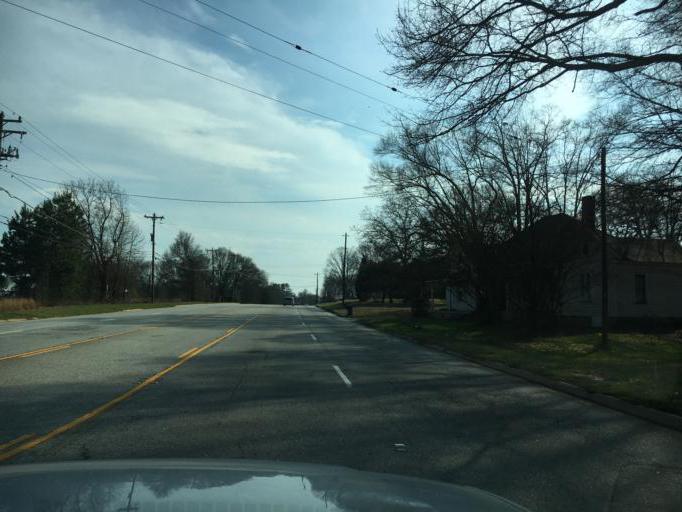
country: US
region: South Carolina
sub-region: Spartanburg County
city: Mayo
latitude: 35.0441
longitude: -81.8909
